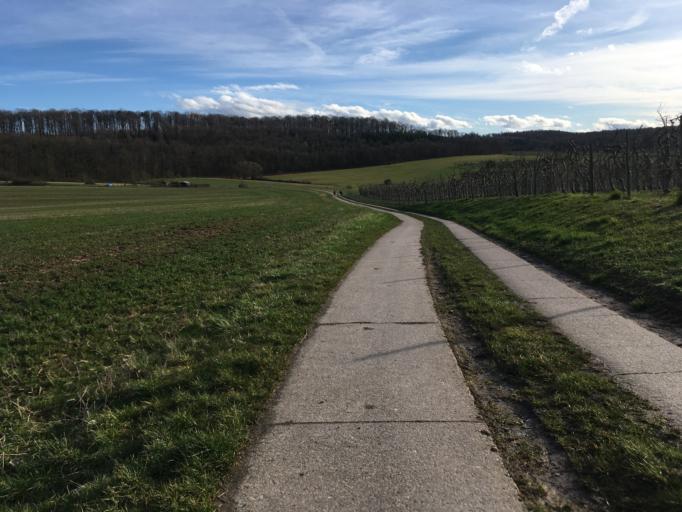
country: DE
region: Baden-Wuerttemberg
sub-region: Regierungsbezirk Stuttgart
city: Lehrensteinsfeld
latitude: 49.1284
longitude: 9.3372
